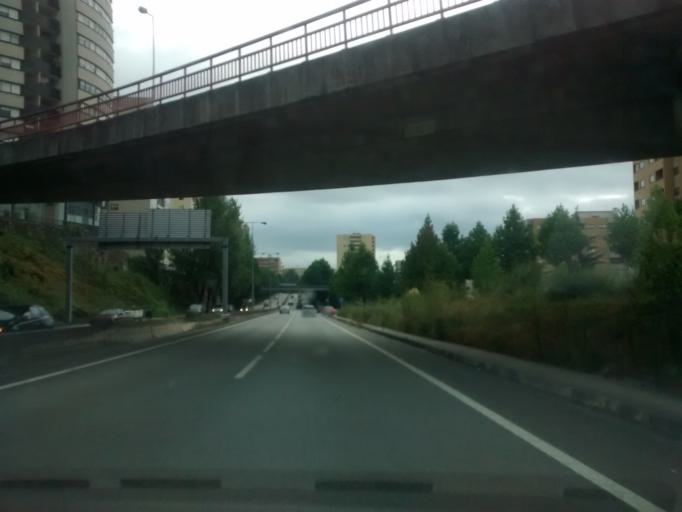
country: PT
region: Braga
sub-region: Braga
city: Braga
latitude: 41.5609
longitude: -8.4191
